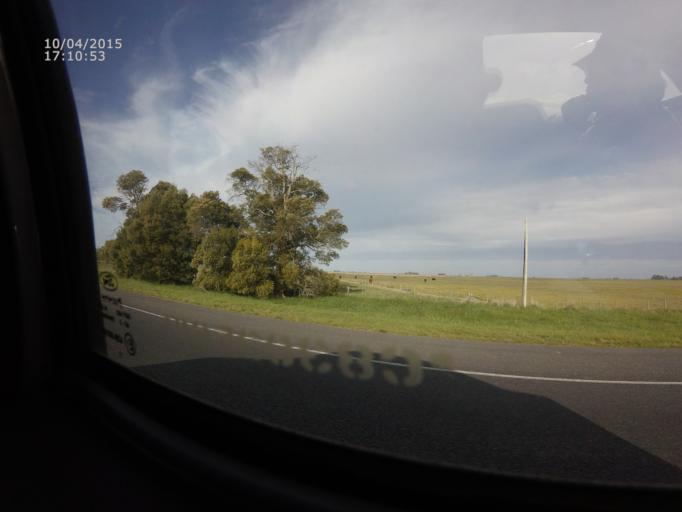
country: AR
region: Buenos Aires
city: Coronel Vidal
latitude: -37.2895
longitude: -57.7725
